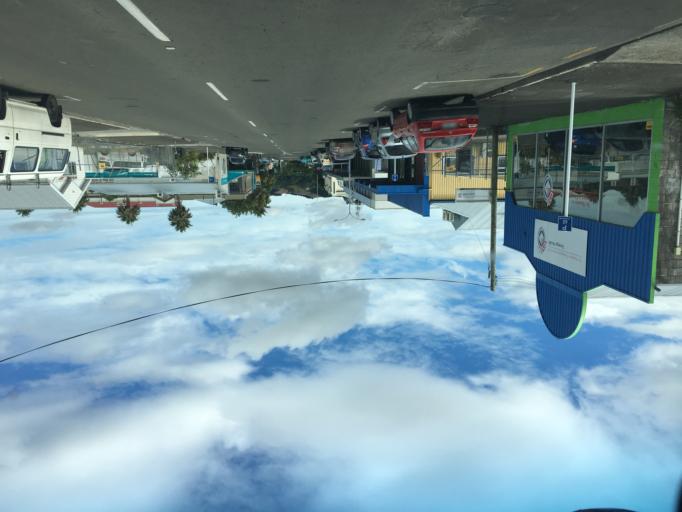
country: NZ
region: Gisborne
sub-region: Gisborne District
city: Gisborne
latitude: -38.6649
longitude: 178.0217
